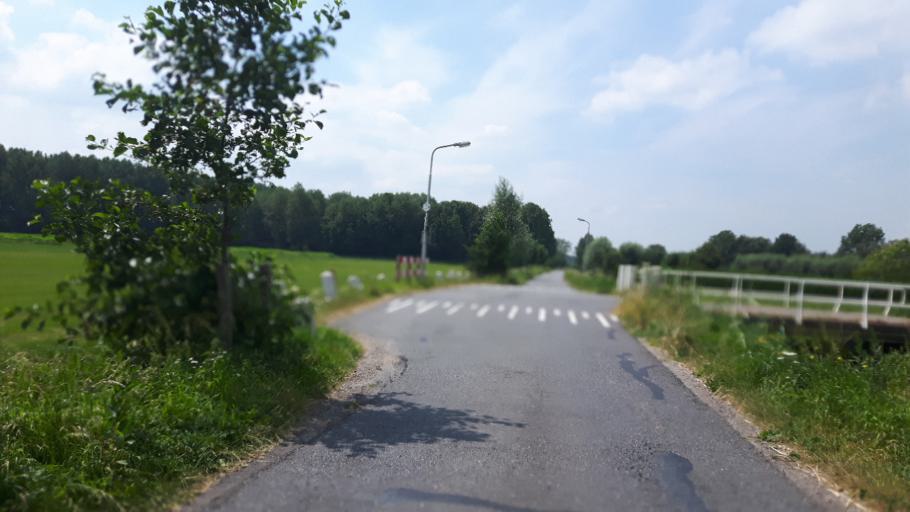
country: NL
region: Utrecht
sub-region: Gemeente Lopik
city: Lopik
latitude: 51.9168
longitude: 4.9772
